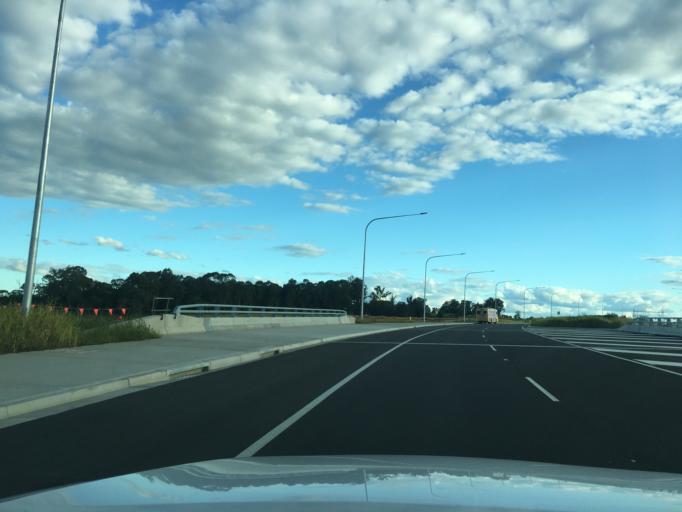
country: AU
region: New South Wales
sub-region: Liverpool
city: Bringelly
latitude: -33.8756
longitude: 150.7499
